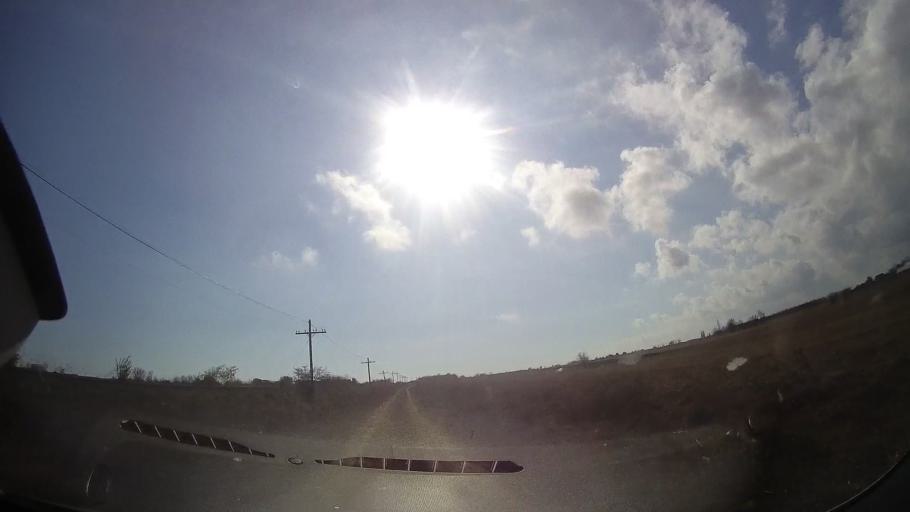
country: RO
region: Constanta
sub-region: Comuna Tuzla
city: Tuzla
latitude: 43.9936
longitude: 28.6452
